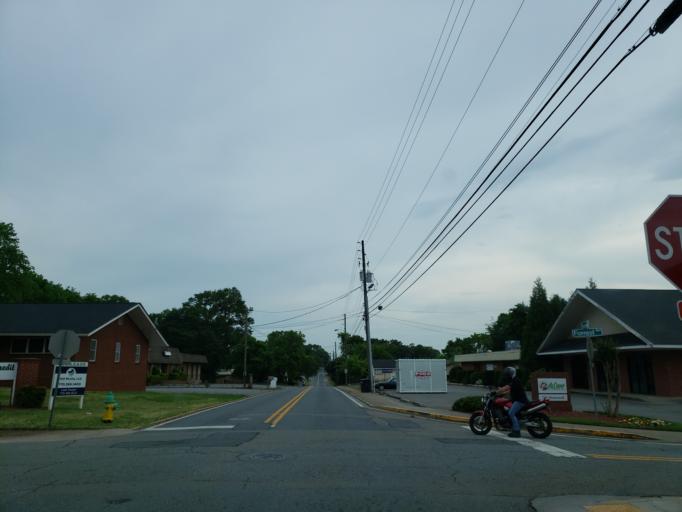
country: US
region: Georgia
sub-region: Bartow County
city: Cartersville
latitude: 34.1653
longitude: -84.7917
